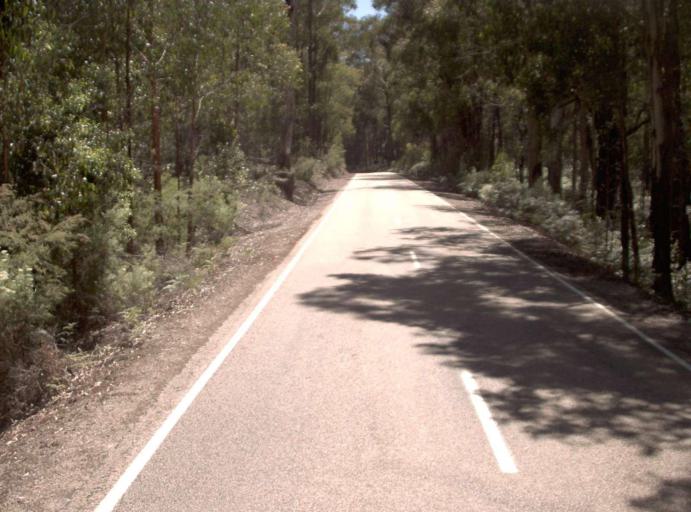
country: AU
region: Victoria
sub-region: East Gippsland
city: Lakes Entrance
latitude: -37.2970
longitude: 148.2497
